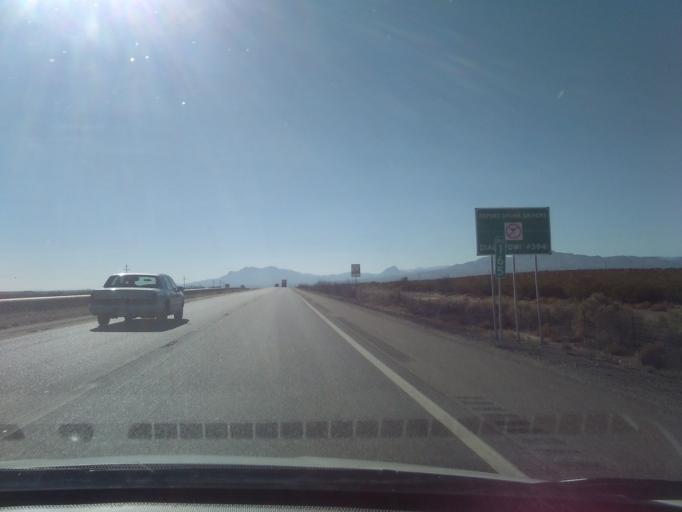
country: US
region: New Mexico
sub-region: Socorro County
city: Socorro
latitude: 34.2817
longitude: -106.8986
